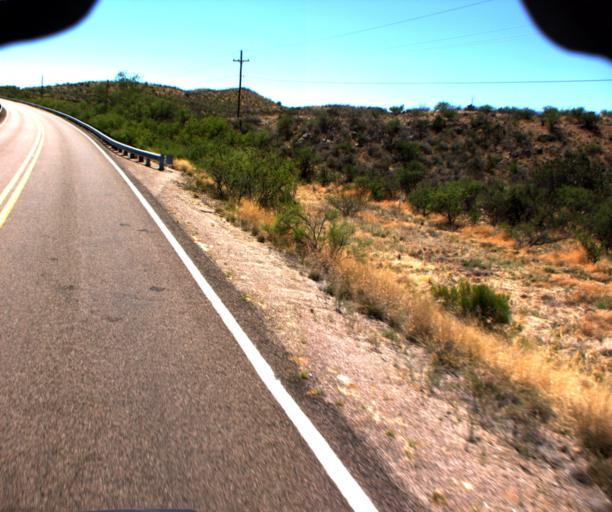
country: US
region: Arizona
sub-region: Pima County
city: Corona de Tucson
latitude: 31.8830
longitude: -110.6742
